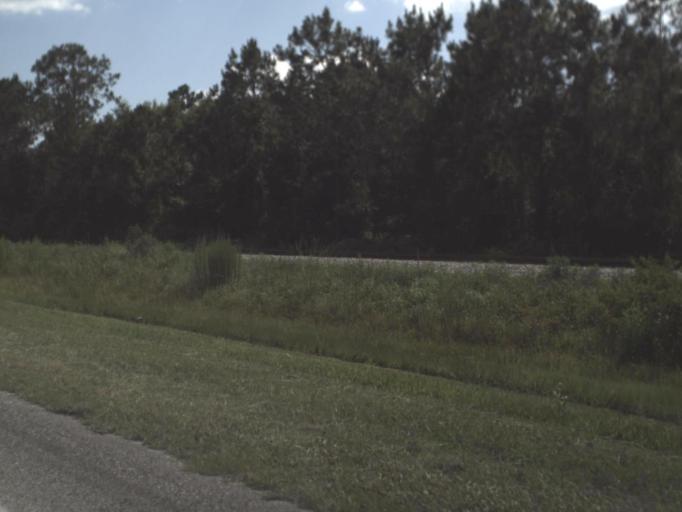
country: US
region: Florida
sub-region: Alachua County
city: Hawthorne
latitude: 29.5330
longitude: -82.1016
